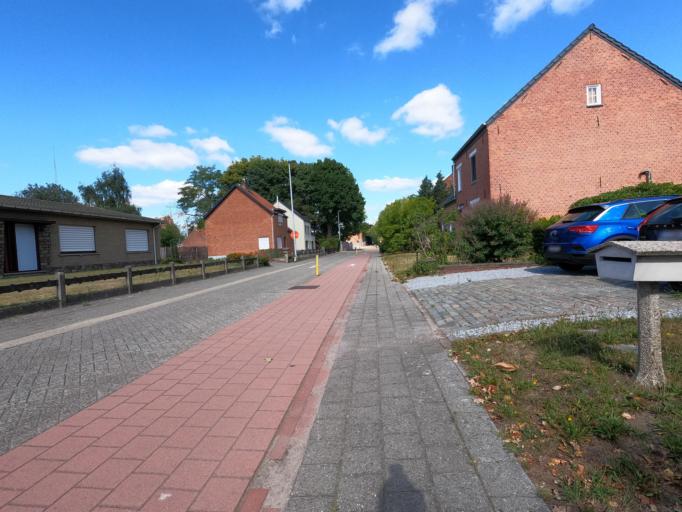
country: BE
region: Flanders
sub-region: Provincie Antwerpen
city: Hulshout
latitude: 51.0853
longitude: 4.8383
